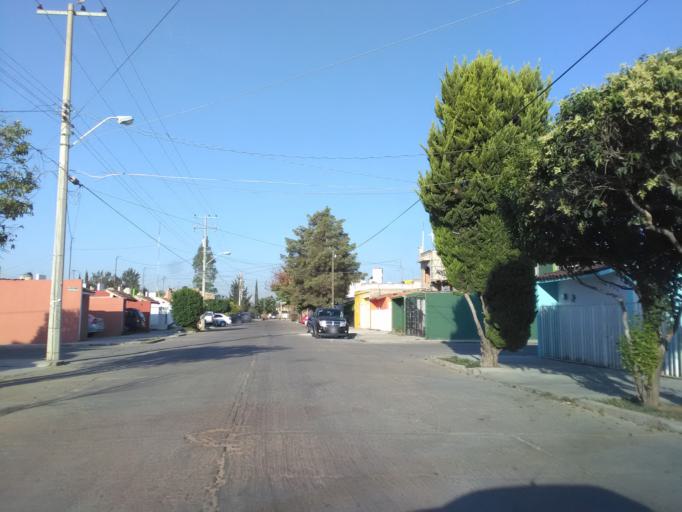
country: MX
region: Durango
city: Victoria de Durango
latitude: 24.0558
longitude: -104.6238
